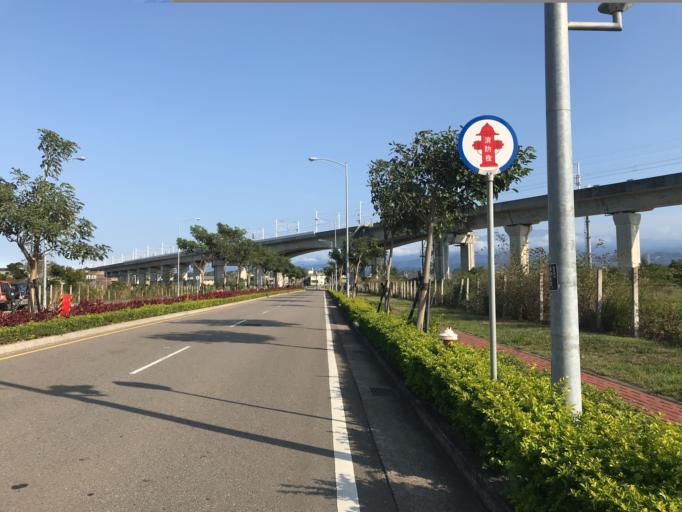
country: TW
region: Taiwan
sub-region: Miaoli
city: Miaoli
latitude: 24.6029
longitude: 120.8168
